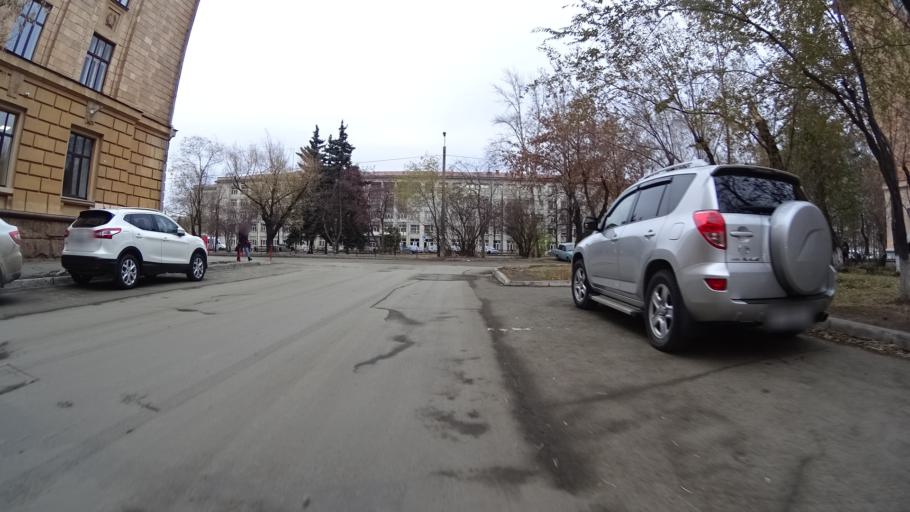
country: RU
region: Chelyabinsk
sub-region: Gorod Chelyabinsk
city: Chelyabinsk
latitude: 55.1601
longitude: 61.3681
